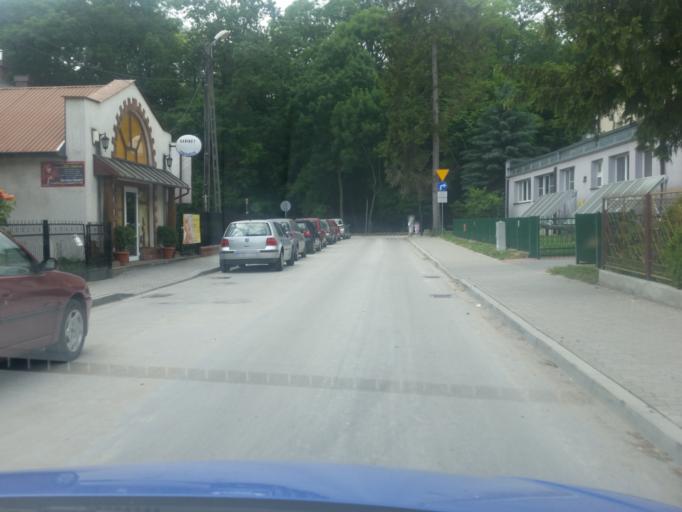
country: PL
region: Swietokrzyskie
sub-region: Powiat buski
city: Busko-Zdroj
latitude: 50.4598
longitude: 20.7228
